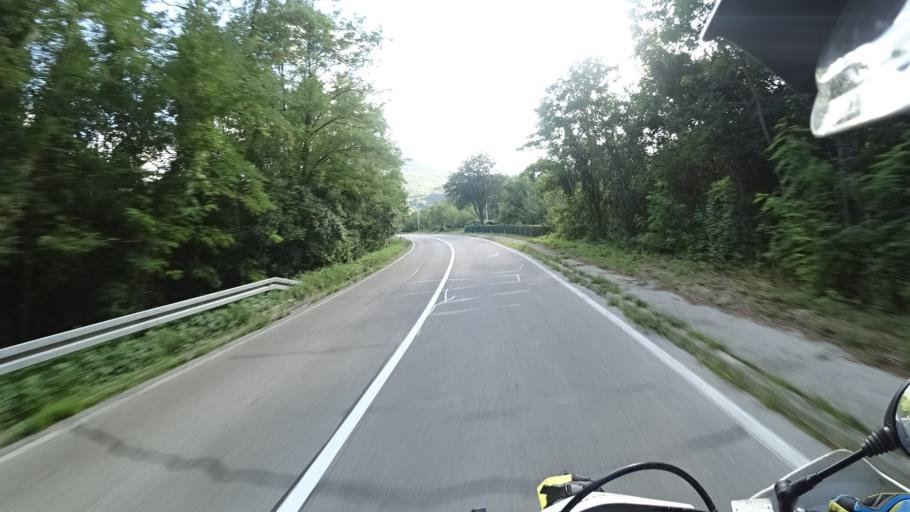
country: HR
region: Zadarska
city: Gracac
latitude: 44.3539
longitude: 16.1170
